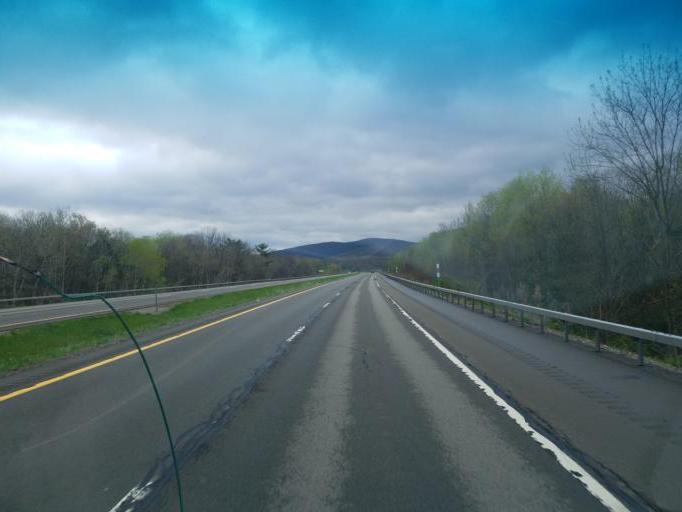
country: US
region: New York
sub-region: Cattaraugus County
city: Randolph
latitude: 42.1028
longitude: -78.8697
